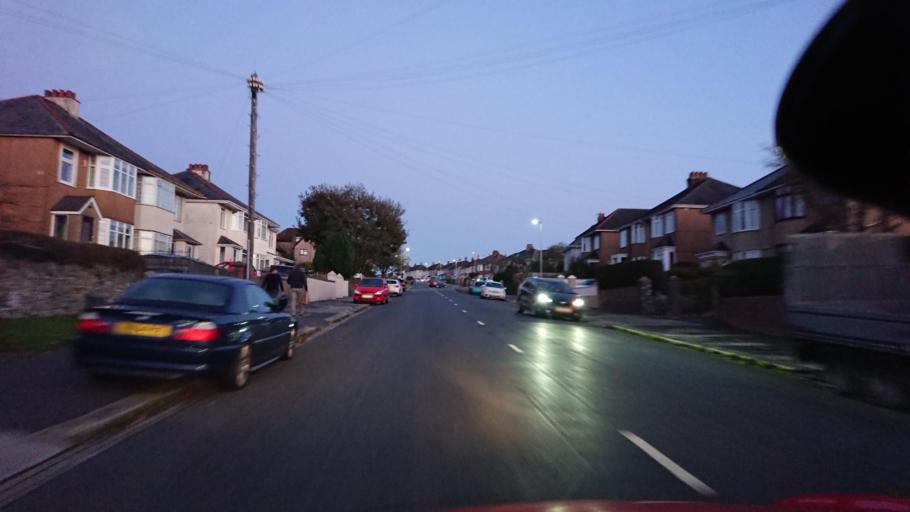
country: GB
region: England
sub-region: Plymouth
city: Plymouth
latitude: 50.3916
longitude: -4.1165
